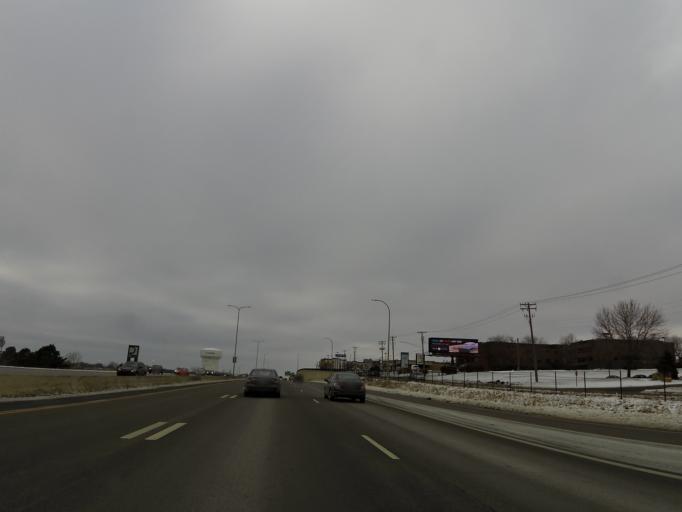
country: US
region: Minnesota
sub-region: Hennepin County
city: Minnetonka Mills
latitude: 44.9713
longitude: -93.4349
